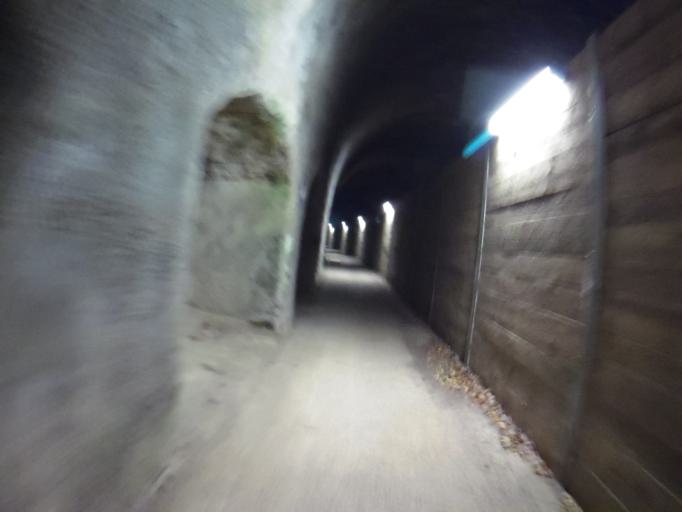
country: DE
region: Rheinland-Pfalz
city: Hosten
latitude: 49.8783
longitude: 6.6061
